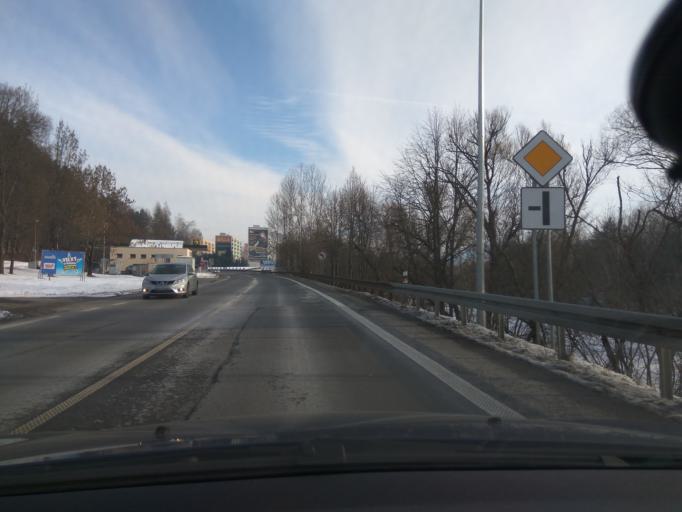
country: SK
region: Banskobystricky
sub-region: Okres Banska Bystrica
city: Brezno
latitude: 48.8060
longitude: 19.6189
